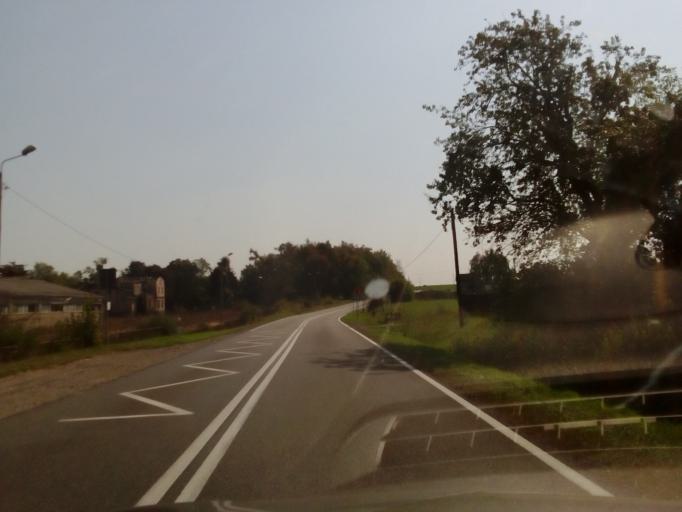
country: PL
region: Kujawsko-Pomorskie
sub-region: Powiat sepolenski
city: Sosno
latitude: 53.4368
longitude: 17.6873
